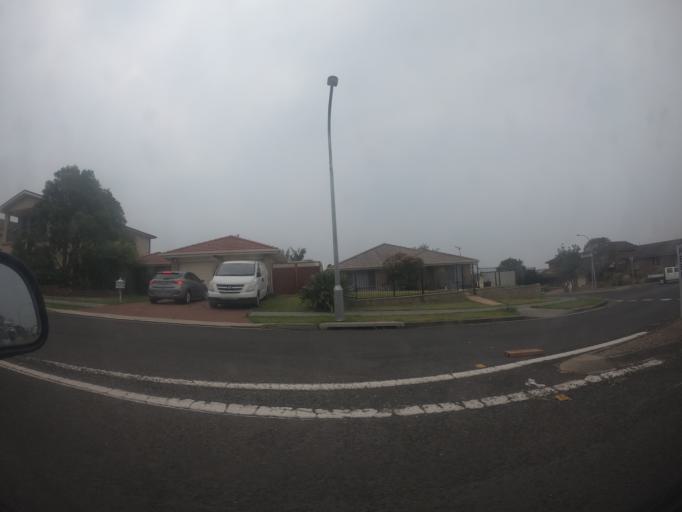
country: AU
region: New South Wales
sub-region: Shellharbour
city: Flinders
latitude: -34.5796
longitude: 150.8444
